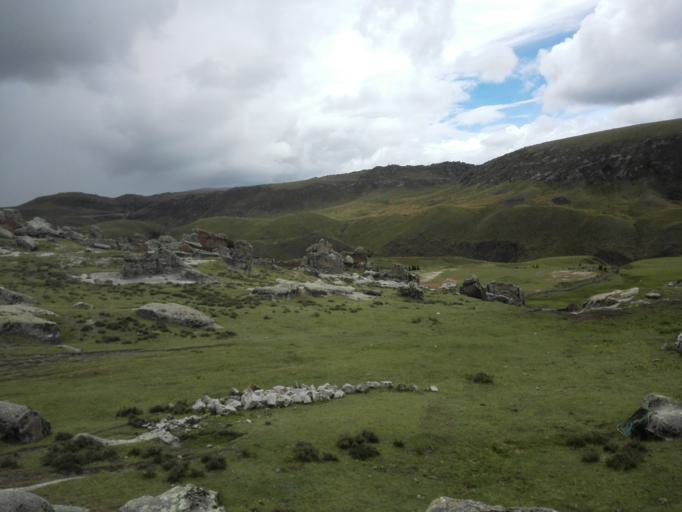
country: PE
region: Ayacucho
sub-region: Provincia de Huamanga
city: Vinchos
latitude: -13.3170
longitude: -74.4499
